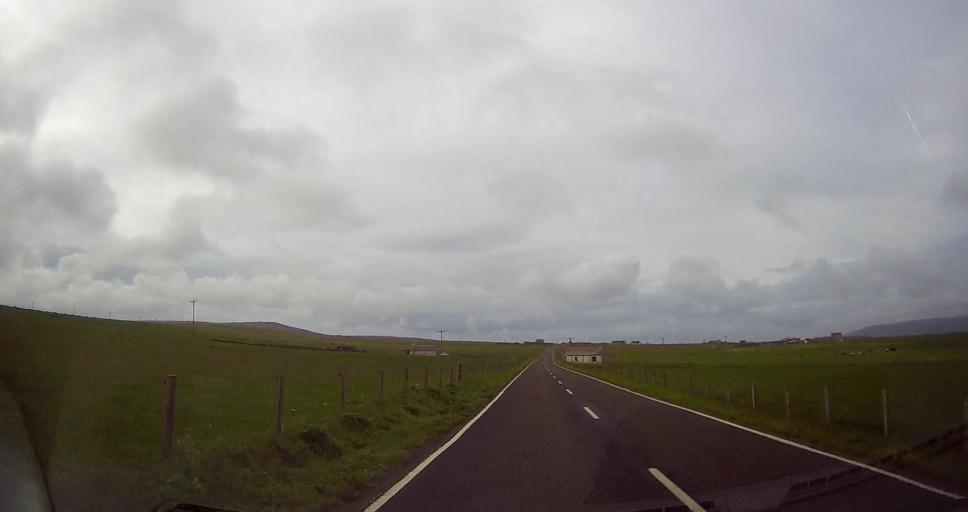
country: GB
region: Scotland
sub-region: Orkney Islands
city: Stromness
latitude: 58.9629
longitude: -3.2237
